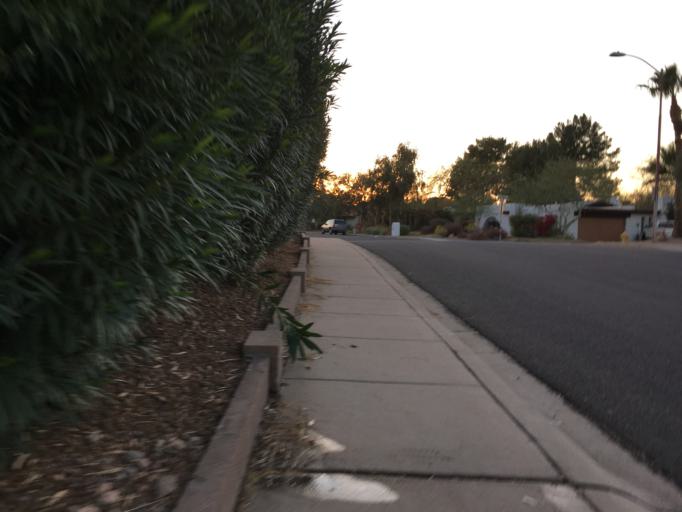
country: US
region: Arizona
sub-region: Maricopa County
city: Paradise Valley
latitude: 33.5721
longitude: -112.0086
